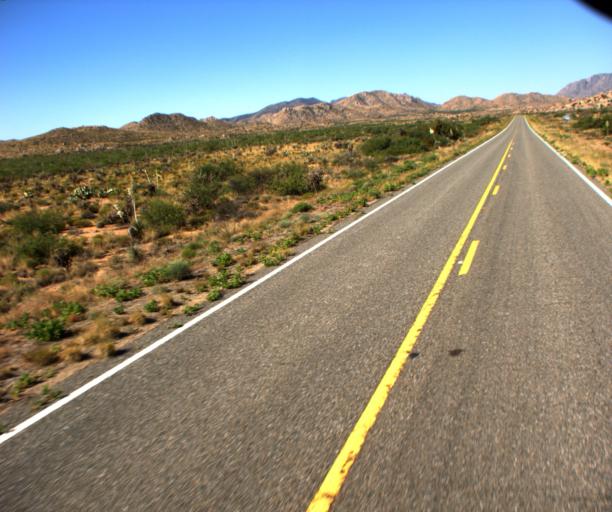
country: US
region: Arizona
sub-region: Graham County
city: Swift Trail Junction
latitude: 32.5822
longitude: -109.7057
